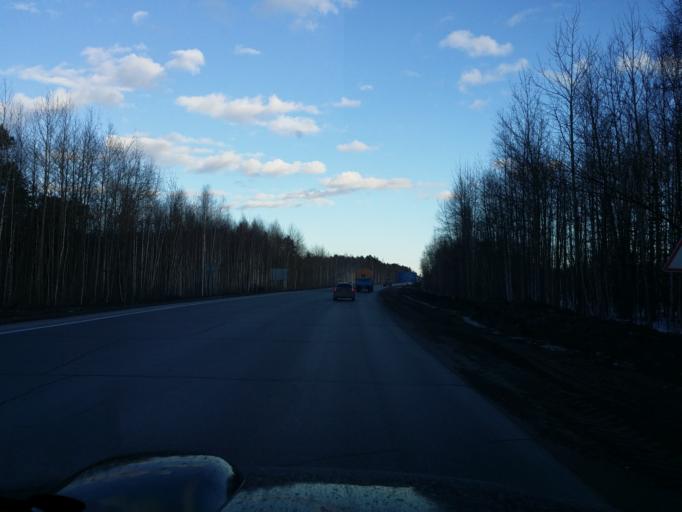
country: RU
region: Khanty-Mansiyskiy Avtonomnyy Okrug
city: Nizhnevartovsk
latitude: 61.0159
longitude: 76.3915
